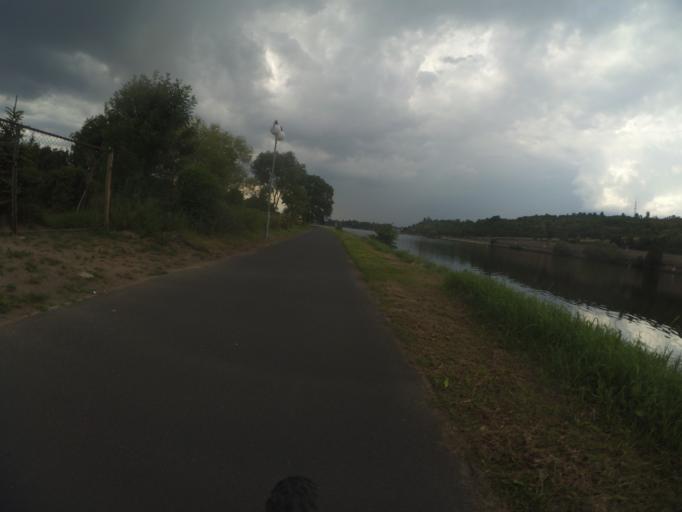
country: CZ
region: Central Bohemia
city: Dolni Berkovice
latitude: 50.3963
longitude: 14.4543
